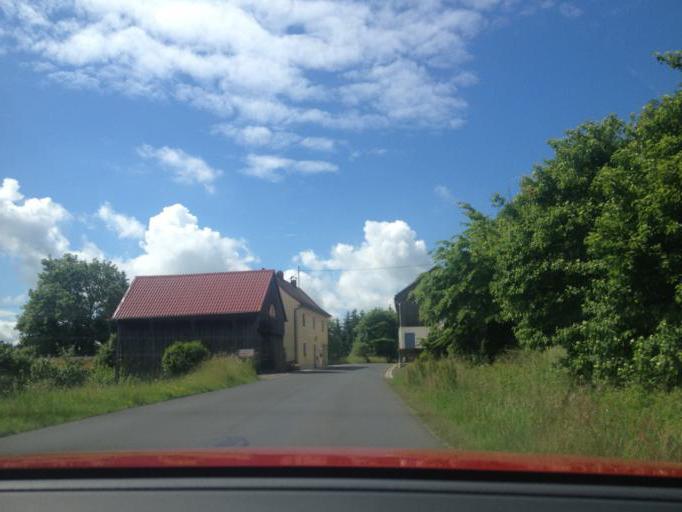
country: DE
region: Bavaria
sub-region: Upper Palatinate
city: Pechbrunn
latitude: 50.0021
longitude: 12.1931
